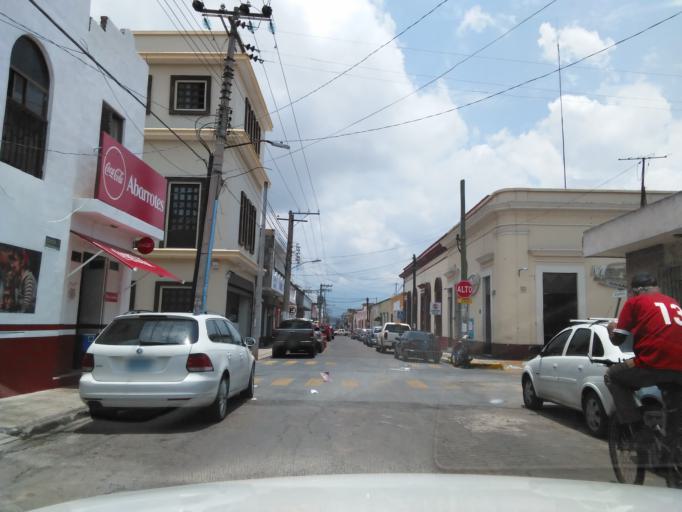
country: MX
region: Nayarit
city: Tepic
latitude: 21.5124
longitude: -104.8985
